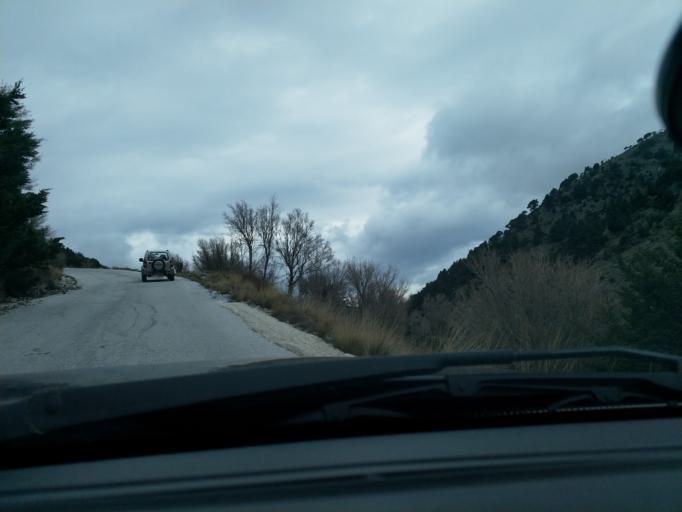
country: GR
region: Crete
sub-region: Nomos Chanias
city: Perivolia
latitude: 35.3083
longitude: 23.9178
